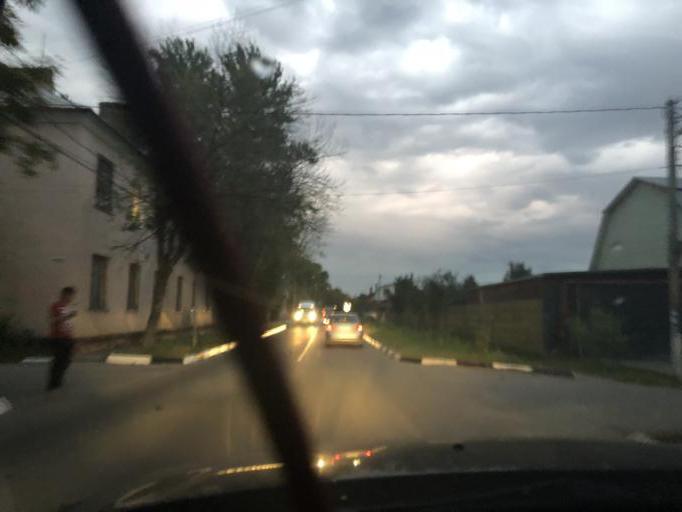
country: RU
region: Tula
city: Tula
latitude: 54.2261
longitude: 37.6209
